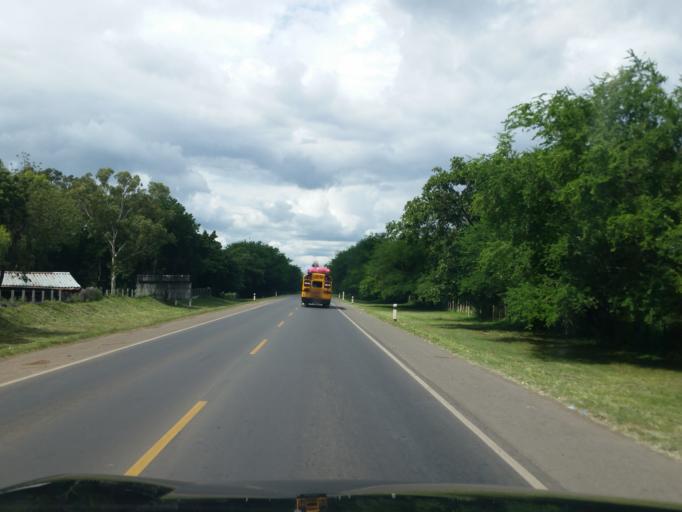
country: NI
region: Managua
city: Tipitapa
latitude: 12.2126
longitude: -86.0992
